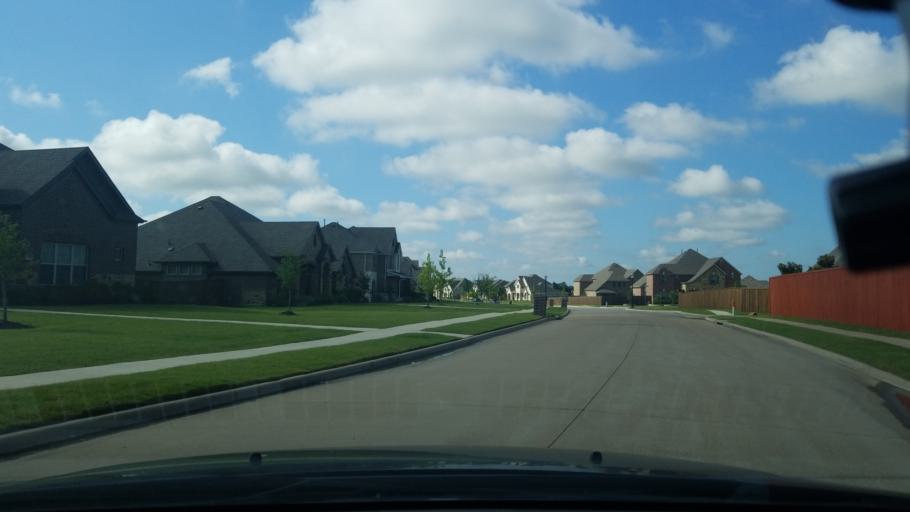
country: US
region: Texas
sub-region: Dallas County
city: Sunnyvale
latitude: 32.8041
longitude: -96.5669
